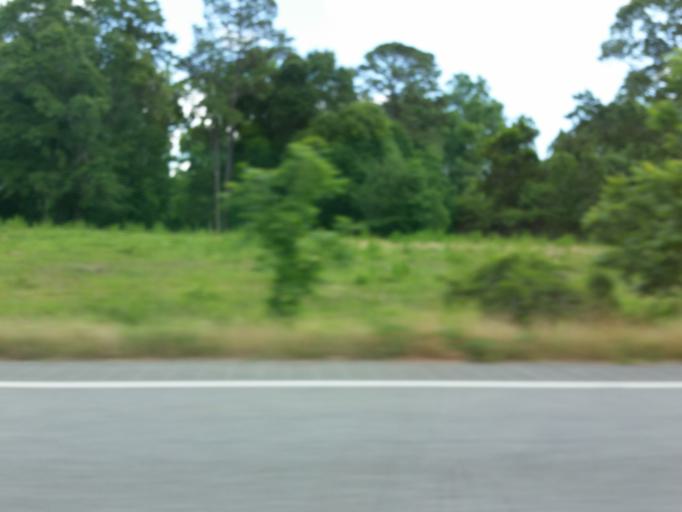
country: US
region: Alabama
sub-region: Sumter County
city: York
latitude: 32.3879
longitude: -88.1989
